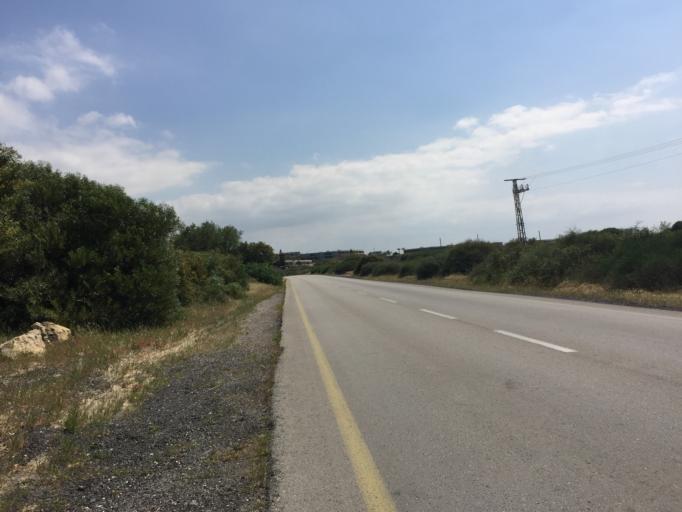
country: IL
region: Haifa
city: Qesarya
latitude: 32.4928
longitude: 34.8988
